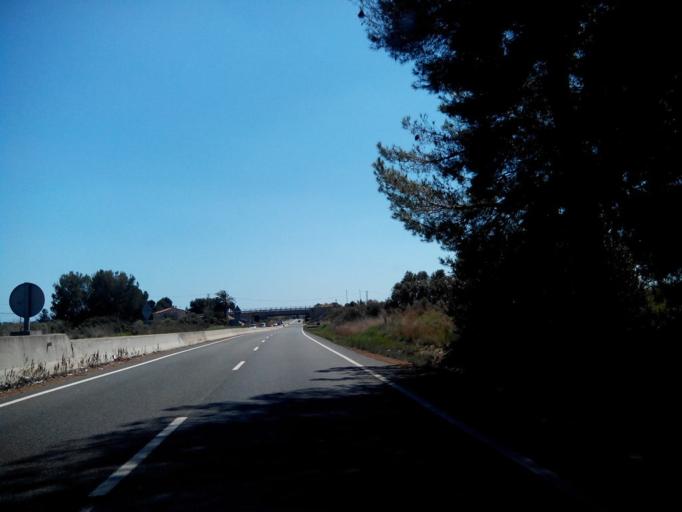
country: ES
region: Catalonia
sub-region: Provincia de Tarragona
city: Vila-seca
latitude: 41.1009
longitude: 1.1278
